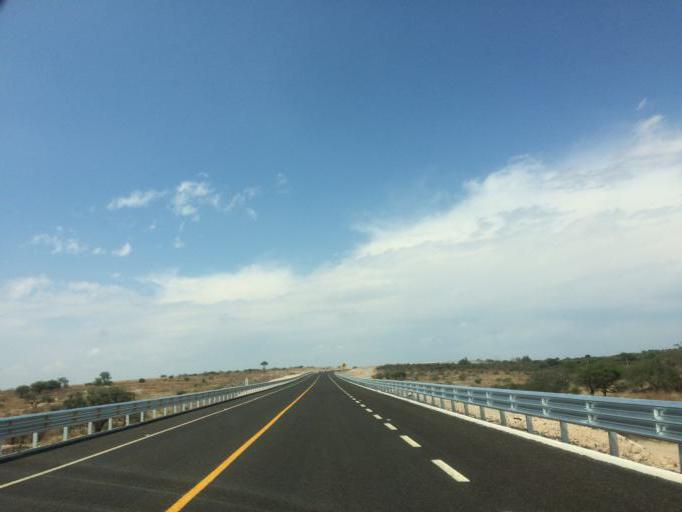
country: MX
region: Guanajuato
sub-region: Silao de la Victoria
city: El Refugio de los Sauces
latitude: 21.0333
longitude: -101.4972
